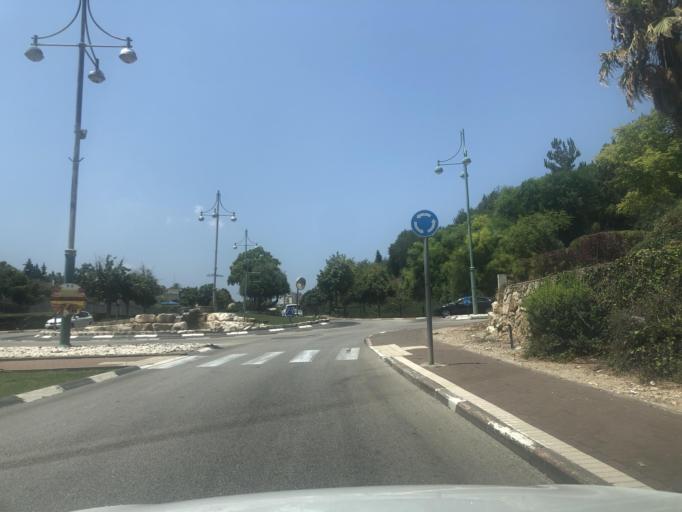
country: IL
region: Haifa
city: Daliyat el Karmil
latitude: 32.6417
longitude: 35.0898
